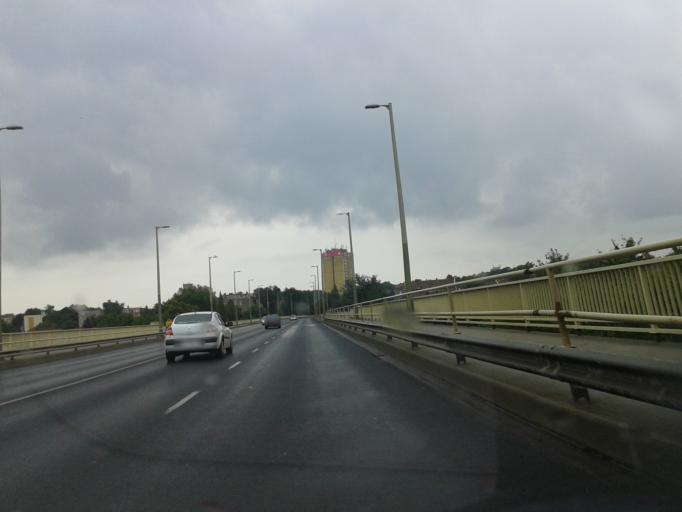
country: HU
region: Csongrad
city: Szeged
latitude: 46.2551
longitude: 20.1655
